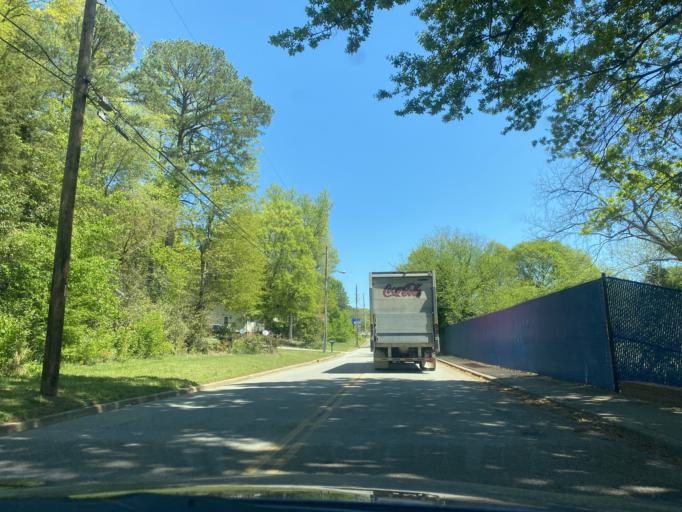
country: US
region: South Carolina
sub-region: Cherokee County
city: Gaffney
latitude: 35.0575
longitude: -81.6436
